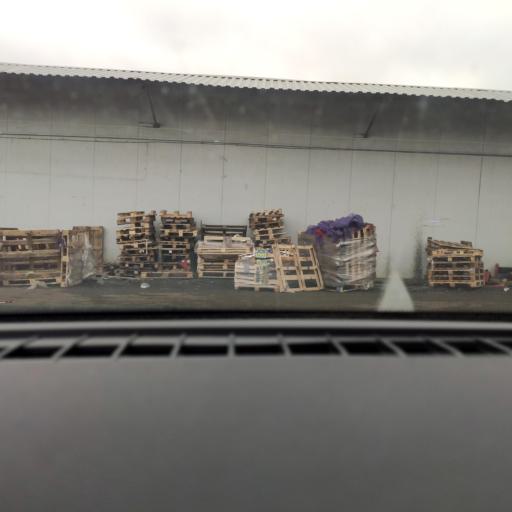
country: RU
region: Voronezj
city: Maslovka
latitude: 51.6111
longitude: 39.2653
